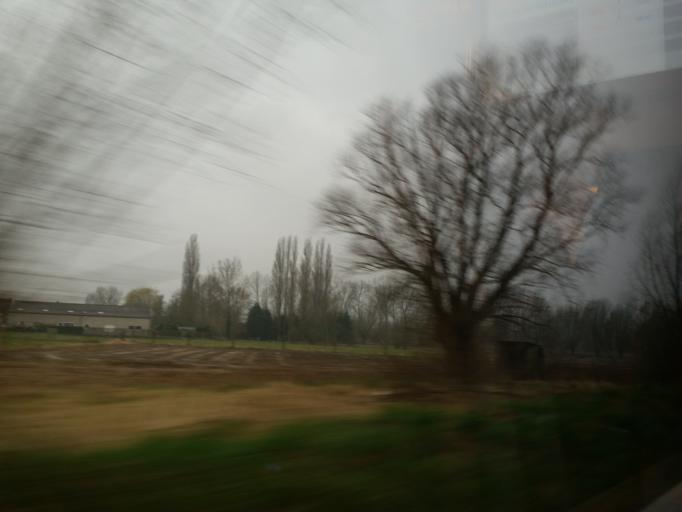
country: BE
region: Flanders
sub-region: Provincie Oost-Vlaanderen
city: Lebbeke
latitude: 51.0195
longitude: 4.1515
